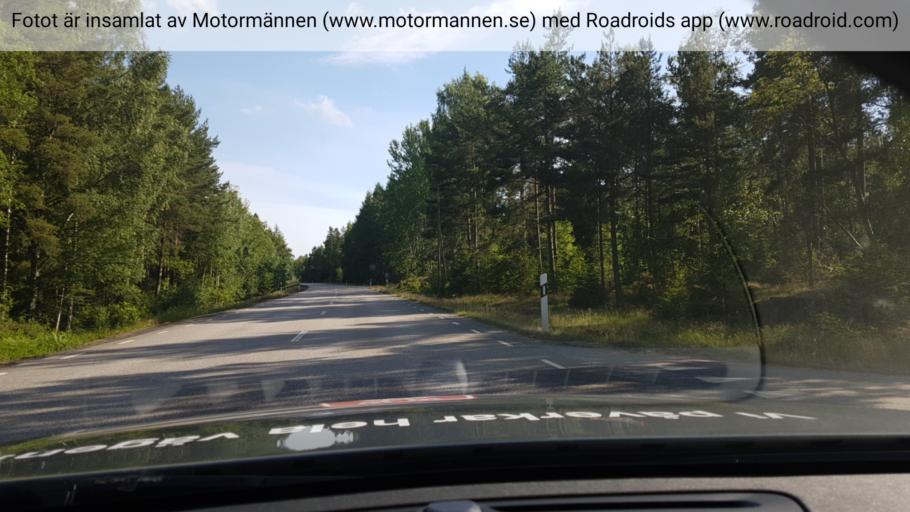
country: SE
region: Vaestra Goetaland
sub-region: Karlsborgs Kommun
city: Karlsborg
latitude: 58.6194
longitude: 14.5323
